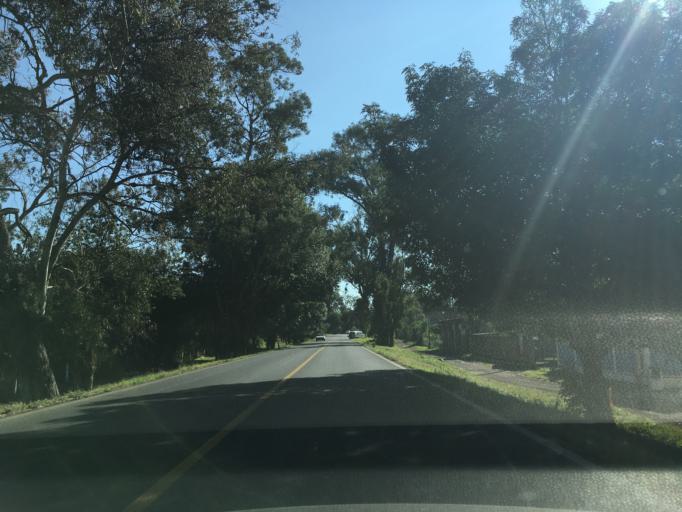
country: MX
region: Mexico
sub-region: Chalco
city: Chilchota
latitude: 19.8504
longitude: -102.1241
